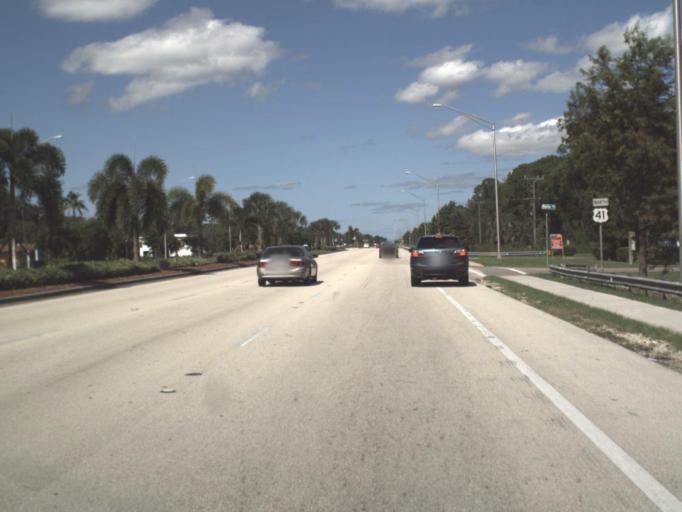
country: US
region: Florida
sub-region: Collier County
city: Naples Manor
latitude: 26.0859
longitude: -81.7284
